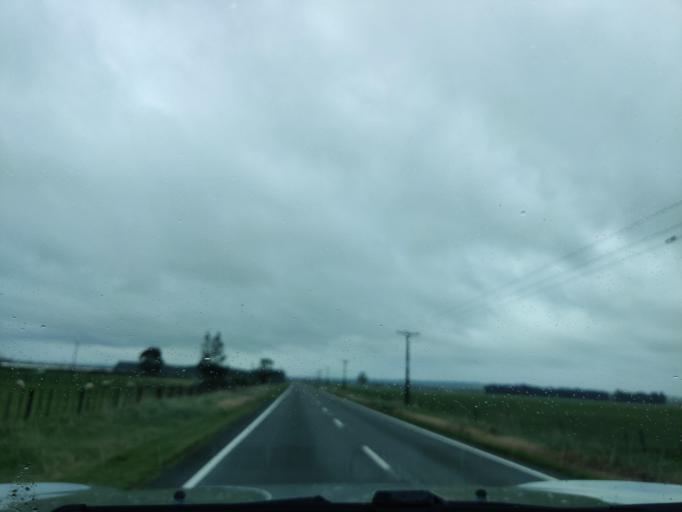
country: NZ
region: Hawke's Bay
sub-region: Hastings District
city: Hastings
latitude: -40.0119
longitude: 176.3711
